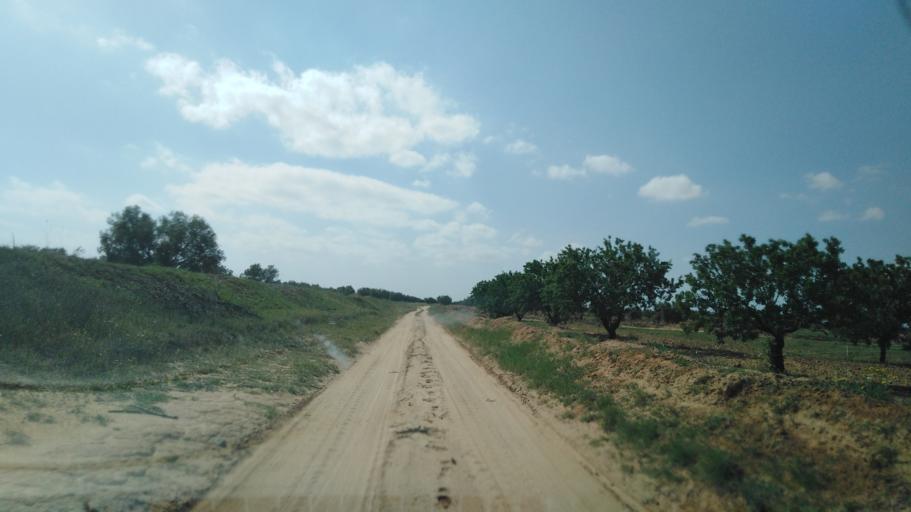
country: TN
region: Safaqis
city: Bi'r `Ali Bin Khalifah
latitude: 34.7913
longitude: 10.4027
